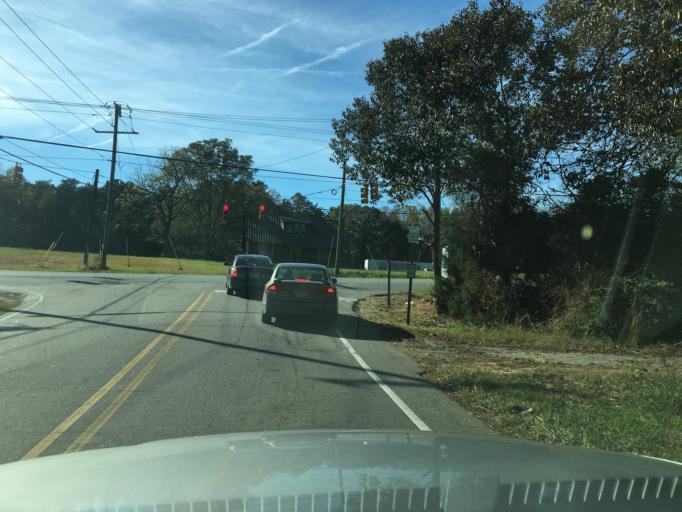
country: US
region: North Carolina
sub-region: Catawba County
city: Saint Stephens
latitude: 35.7111
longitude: -81.2784
